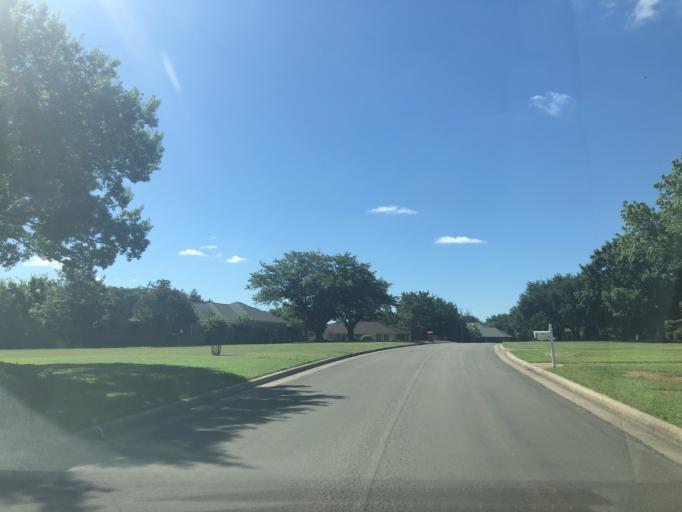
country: US
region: Texas
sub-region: Dallas County
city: Duncanville
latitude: 32.6363
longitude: -96.9394
